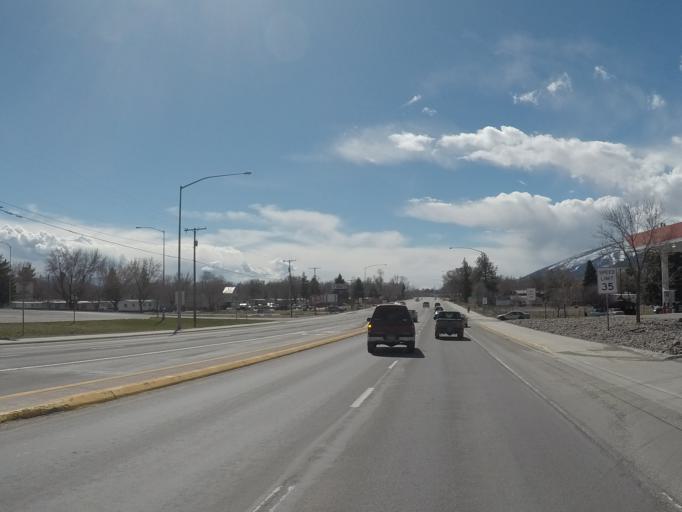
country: US
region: Montana
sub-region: Missoula County
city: Lolo
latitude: 46.7566
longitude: -114.0823
